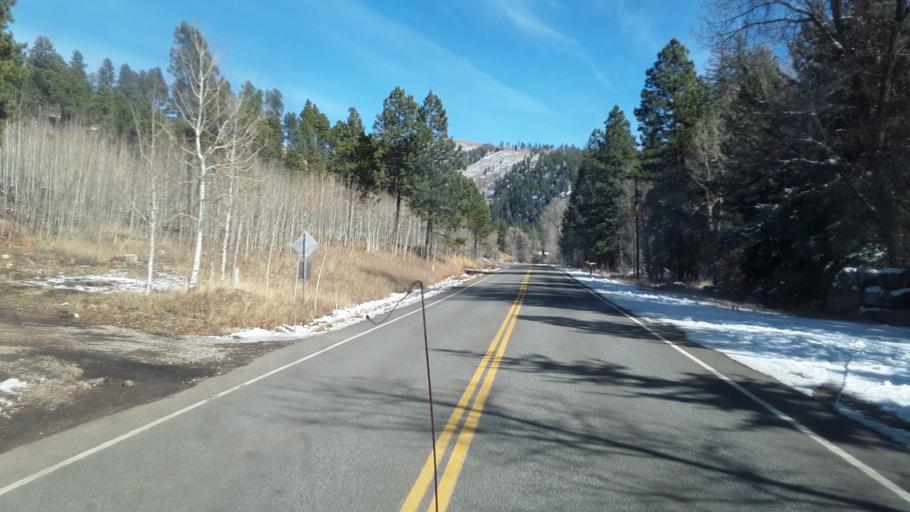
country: US
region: Colorado
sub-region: La Plata County
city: Bayfield
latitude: 37.3585
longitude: -107.6763
